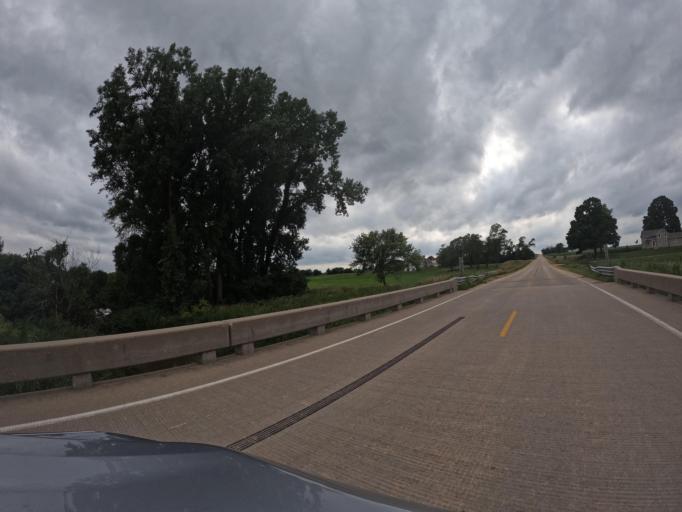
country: US
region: Iowa
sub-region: Clinton County
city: De Witt
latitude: 41.8006
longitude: -90.5168
